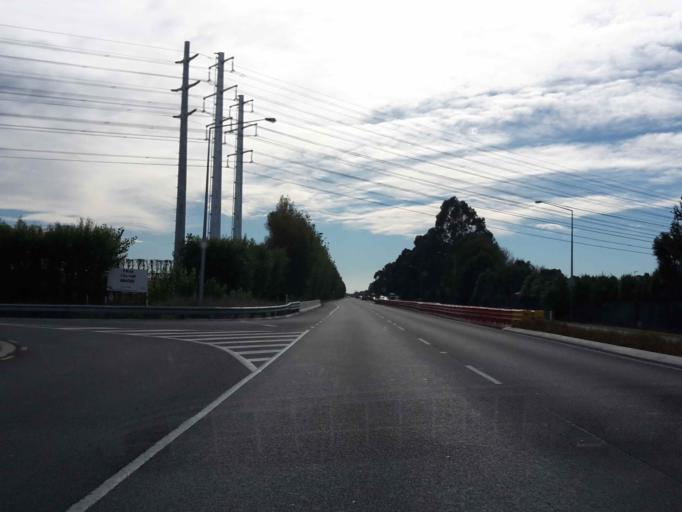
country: NZ
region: Canterbury
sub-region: Selwyn District
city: Prebbleton
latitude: -43.5128
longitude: 172.5384
